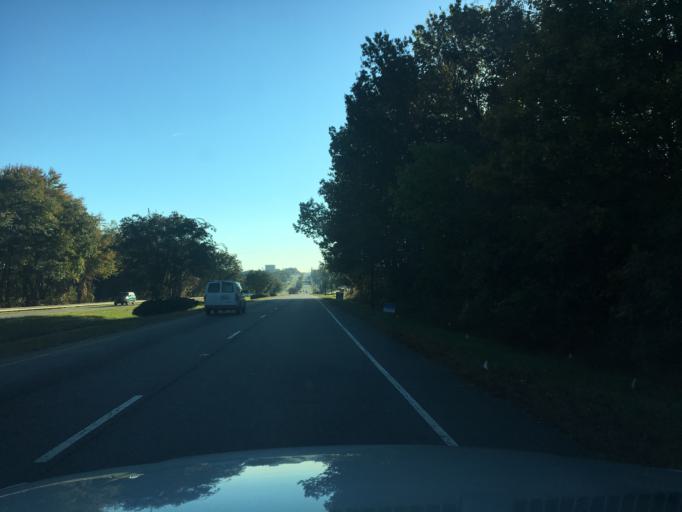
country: US
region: North Carolina
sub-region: Catawba County
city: Hickory
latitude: 35.7304
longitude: -81.3223
